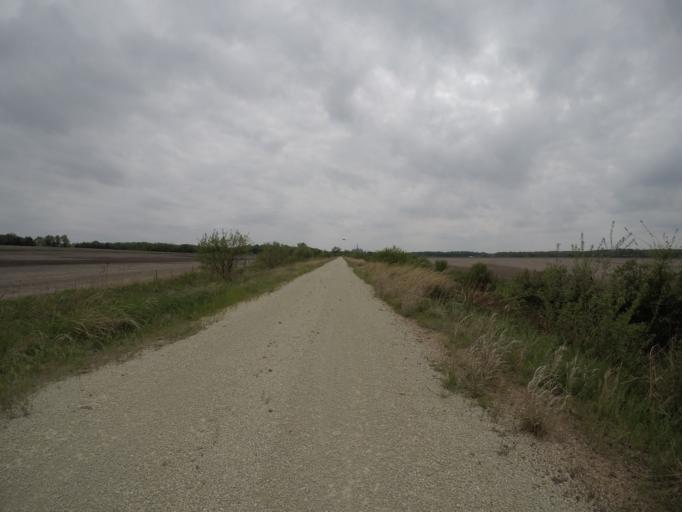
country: US
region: Nebraska
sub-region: Gage County
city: Wymore
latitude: 40.0624
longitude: -96.5800
